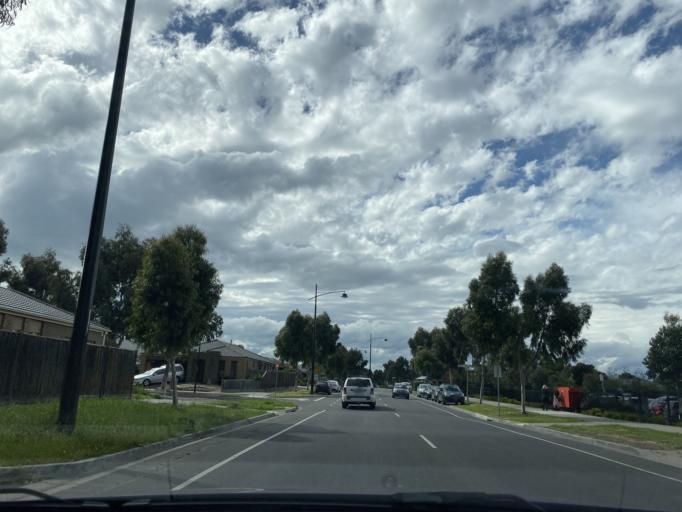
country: AU
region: Victoria
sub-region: Whittlesea
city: Mernda
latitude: -37.6050
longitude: 145.0881
